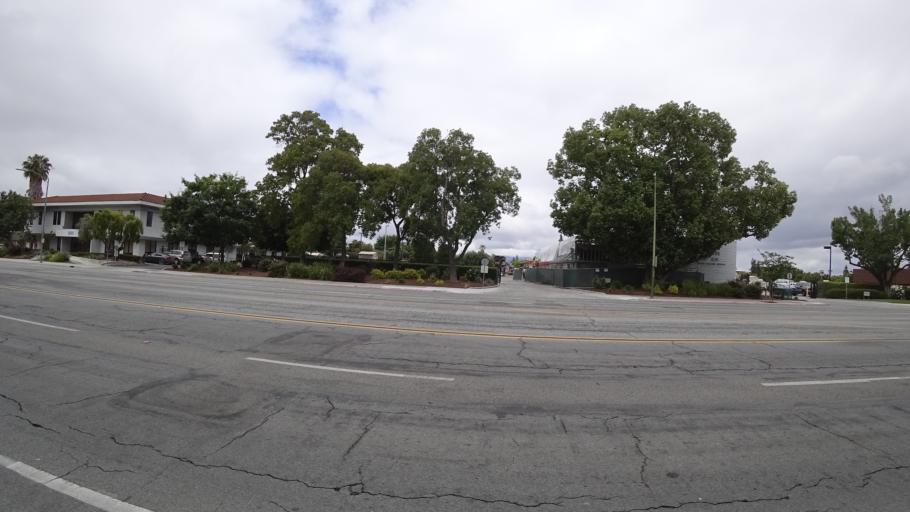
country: US
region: California
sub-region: Santa Clara County
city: Burbank
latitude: 37.3025
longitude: -121.9316
